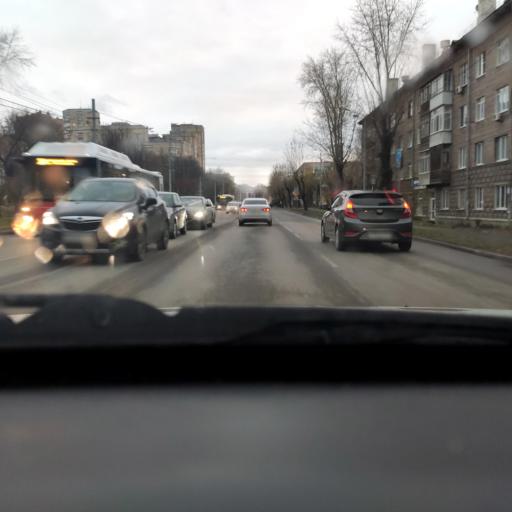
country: RU
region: Perm
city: Perm
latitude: 58.0253
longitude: 56.2899
